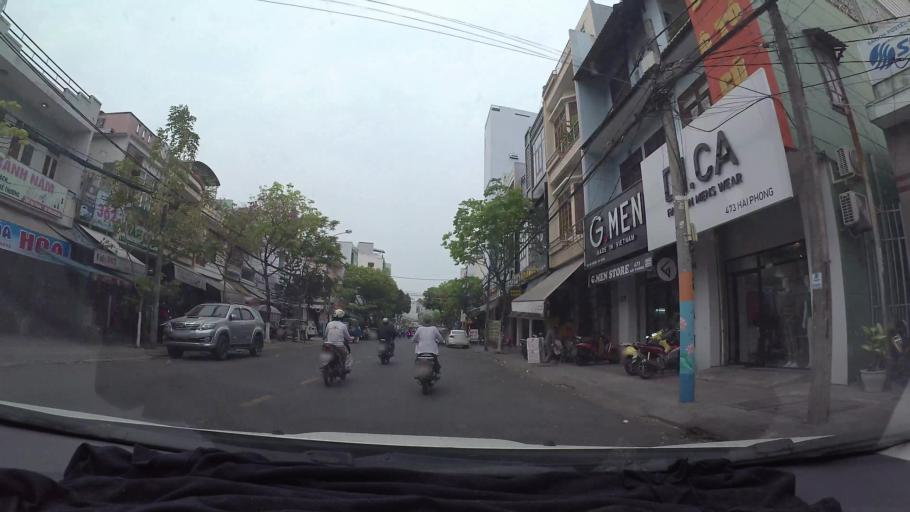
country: VN
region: Da Nang
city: Thanh Khe
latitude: 16.0676
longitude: 108.2051
